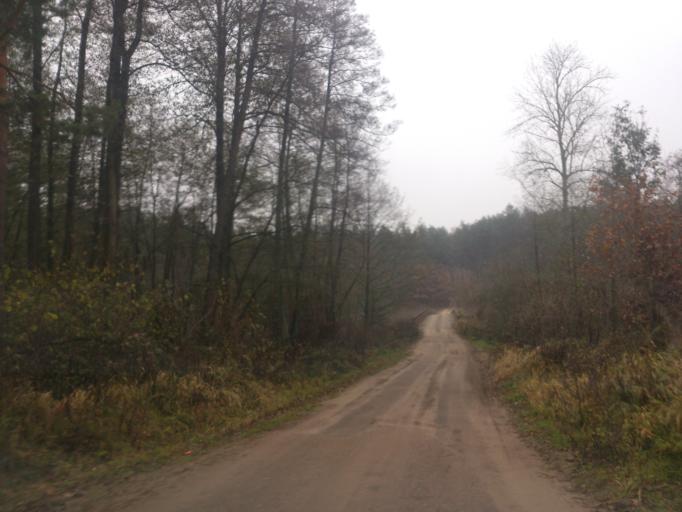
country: PL
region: Kujawsko-Pomorskie
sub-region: Powiat golubsko-dobrzynski
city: Radomin
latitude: 53.1415
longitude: 19.1440
